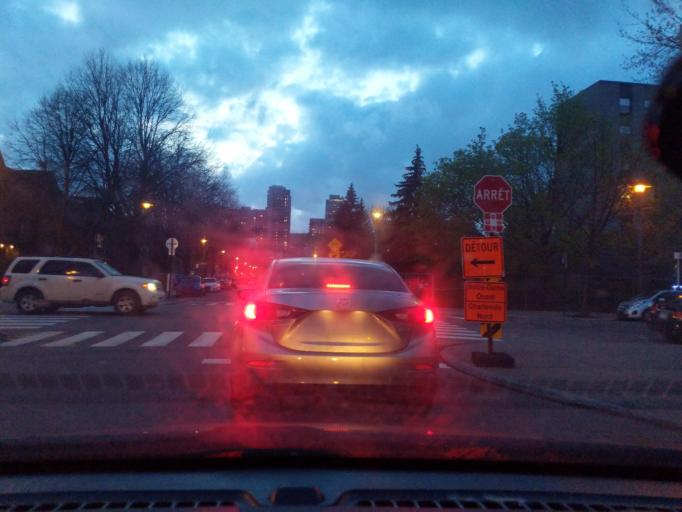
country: CA
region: Quebec
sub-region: Montreal
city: Montreal
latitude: 45.4885
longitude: -73.5709
